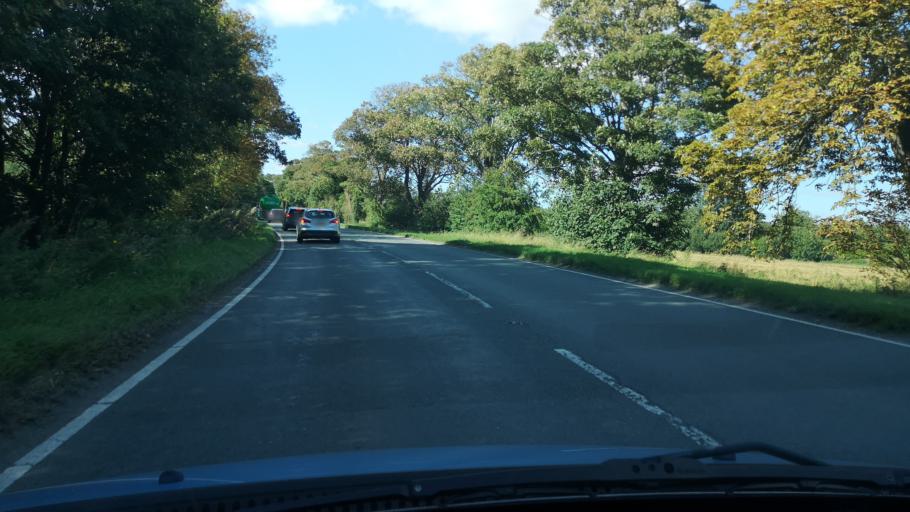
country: GB
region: England
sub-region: North Lincolnshire
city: Belton
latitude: 53.5767
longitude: -0.8182
